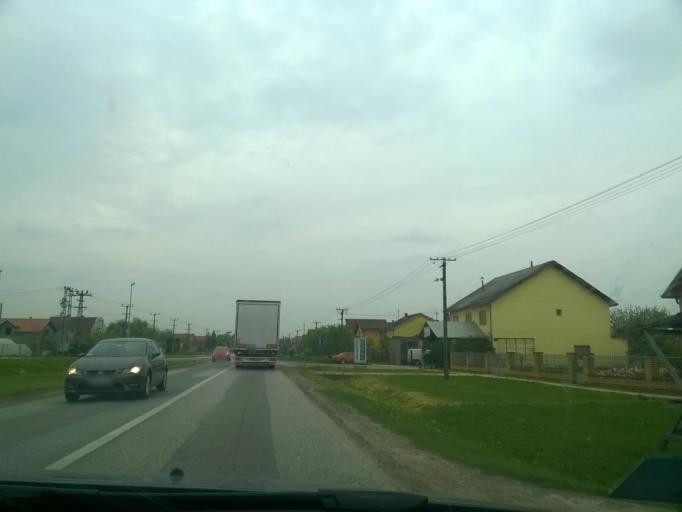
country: RS
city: Hrtkovci
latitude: 44.8909
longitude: 19.7639
